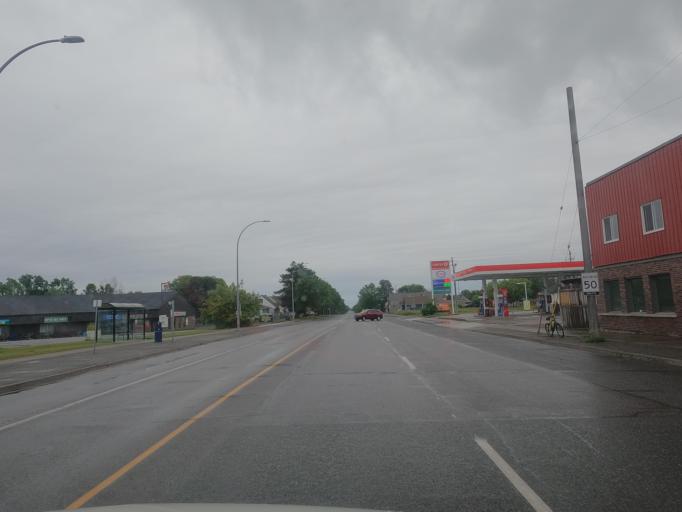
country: CA
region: Ontario
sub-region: Thunder Bay District
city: Thunder Bay
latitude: 48.4688
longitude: -89.1822
